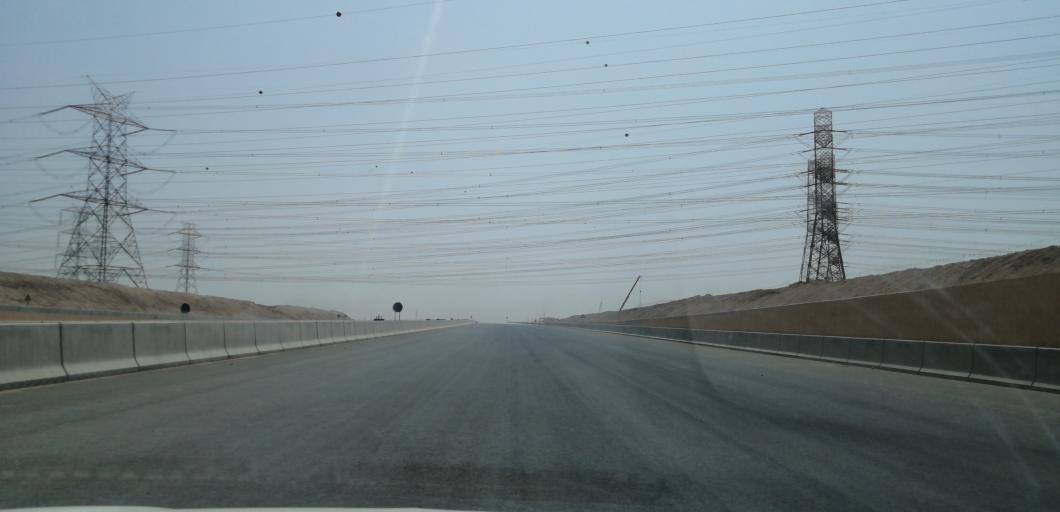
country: KW
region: Muhafazat al Jahra'
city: Al Jahra'
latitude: 29.4475
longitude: 47.6186
